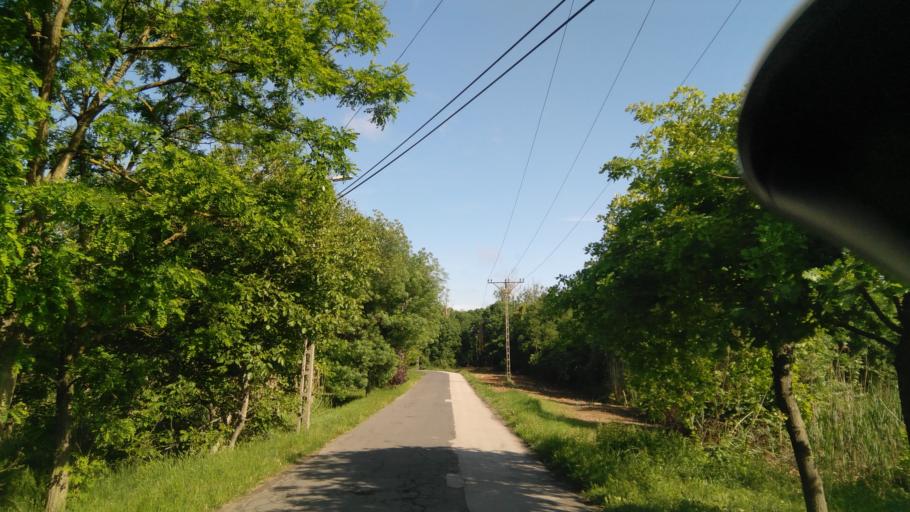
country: HU
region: Bekes
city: Bekes
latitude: 46.7808
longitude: 21.1350
